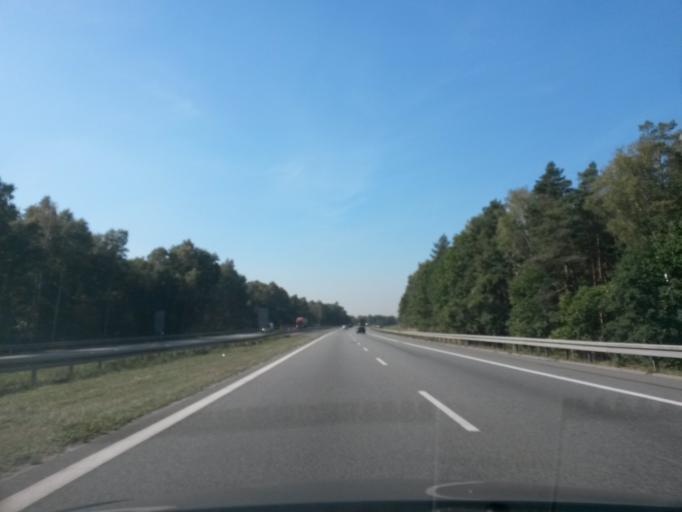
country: PL
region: Silesian Voivodeship
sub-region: Myslowice
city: Myslowice
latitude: 50.2192
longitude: 19.1086
